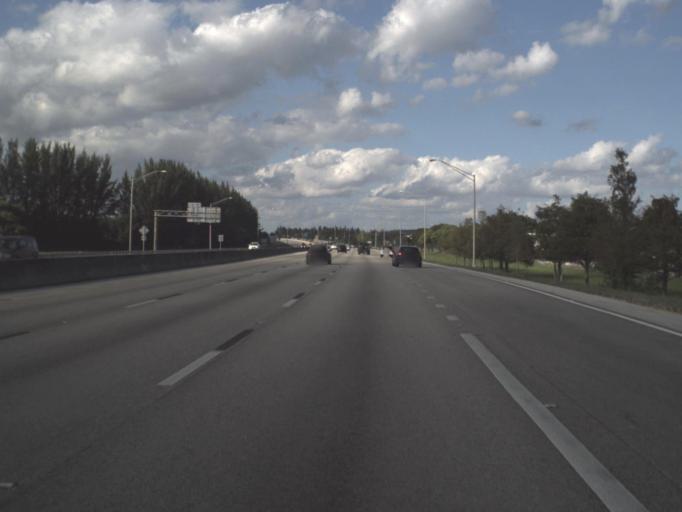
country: US
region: Florida
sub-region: Broward County
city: Coconut Creek
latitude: 26.2515
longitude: -80.1663
